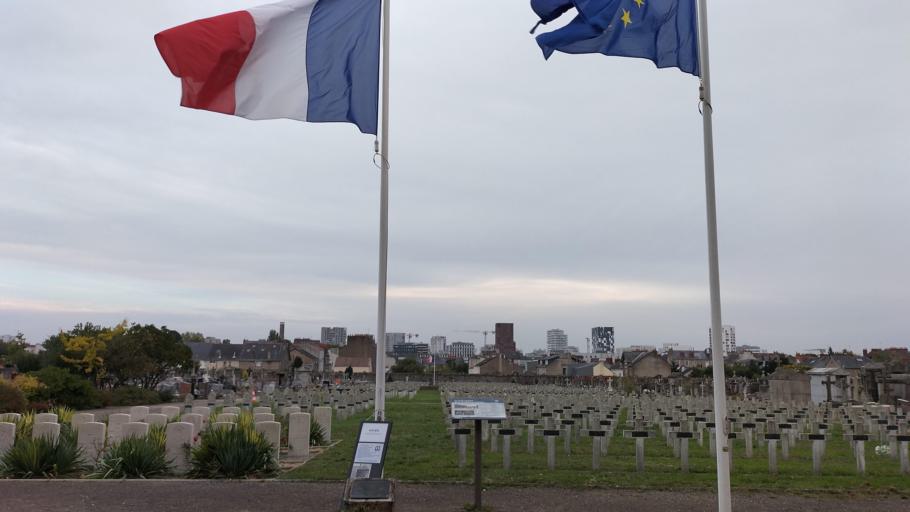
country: FR
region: Pays de la Loire
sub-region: Departement de la Loire-Atlantique
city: Nantes
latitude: 47.2227
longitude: -1.5403
